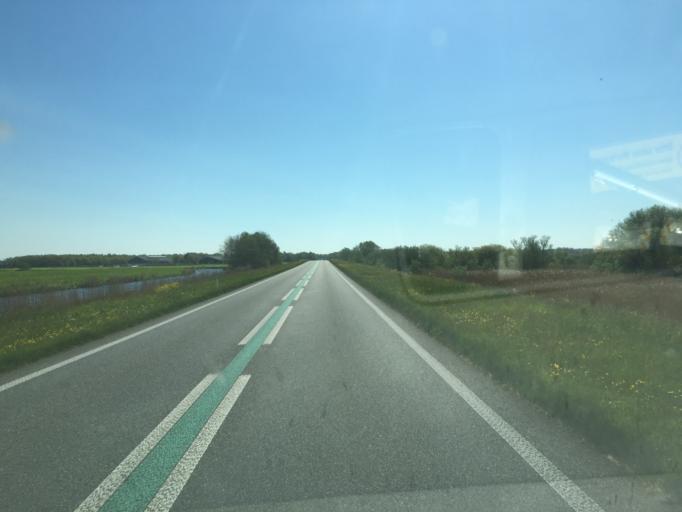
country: NL
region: Friesland
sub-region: Gemeente Gaasterlan-Sleat
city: Oudemirdum
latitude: 52.8813
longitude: 5.4979
